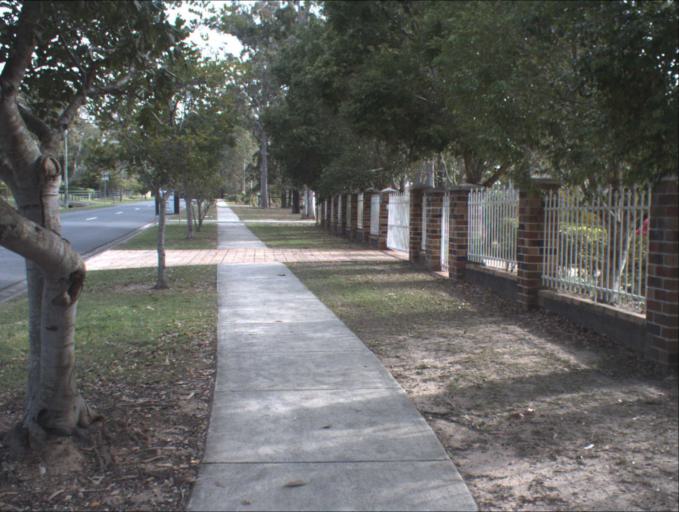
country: AU
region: Queensland
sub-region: Brisbane
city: Forest Lake
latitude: -27.6593
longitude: 153.0008
